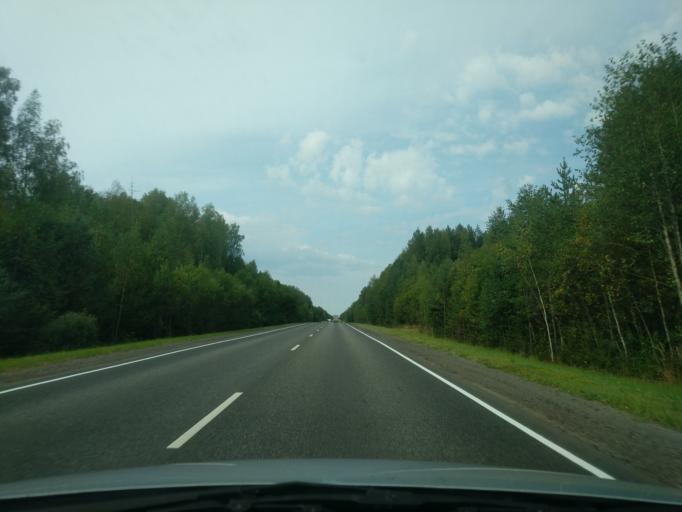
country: RU
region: Kirov
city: Leninskoye
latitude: 58.3188
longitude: 46.8898
